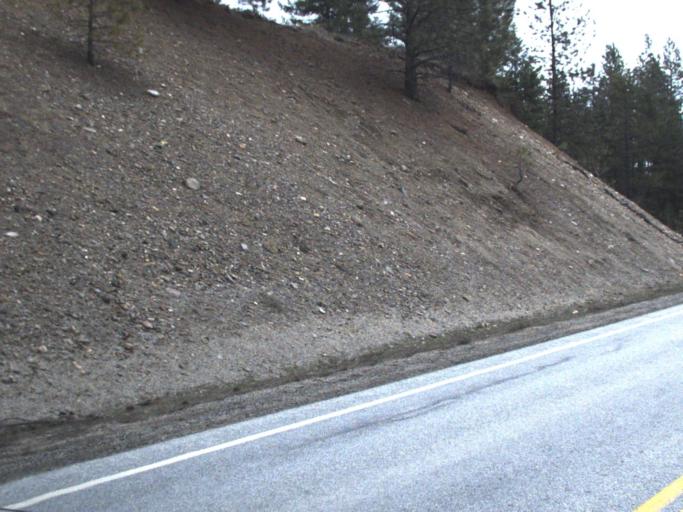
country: US
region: Washington
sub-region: Pend Oreille County
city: Newport
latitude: 48.2198
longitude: -117.0992
